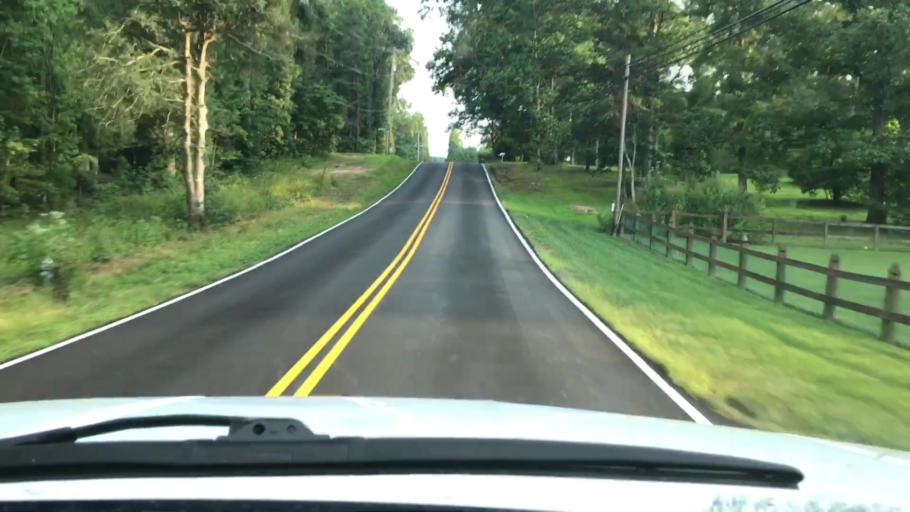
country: US
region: Virginia
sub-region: Chesterfield County
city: Chesterfield
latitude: 37.4230
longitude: -77.5347
